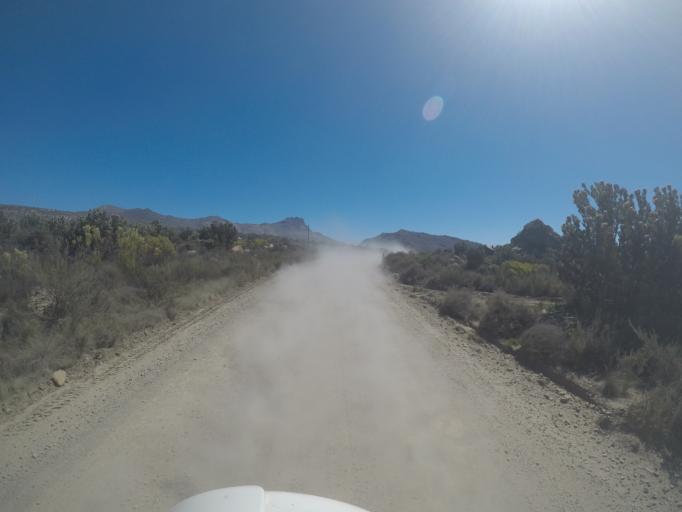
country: ZA
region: Western Cape
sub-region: Cape Winelands District Municipality
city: Ceres
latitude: -32.8757
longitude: 19.4460
